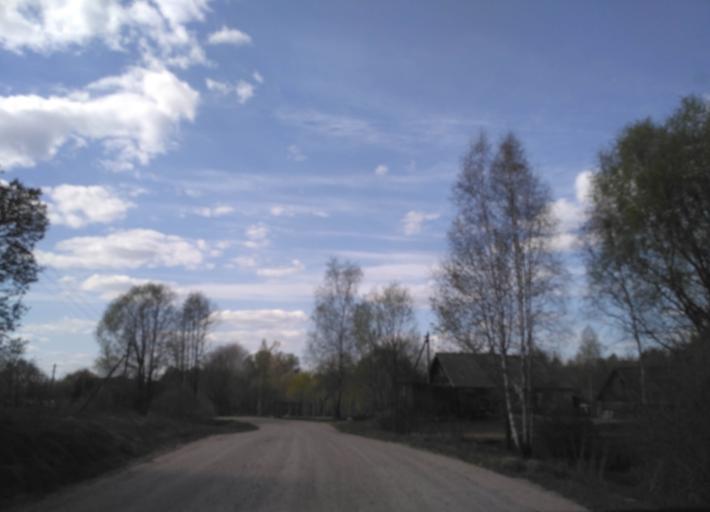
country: BY
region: Minsk
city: Narach
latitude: 54.9887
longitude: 26.5976
